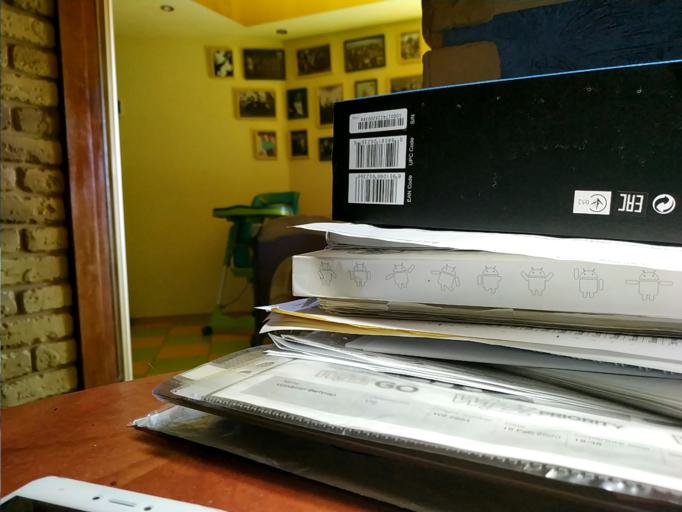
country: RU
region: Vologda
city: Vytegra
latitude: 60.8658
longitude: 36.7352
